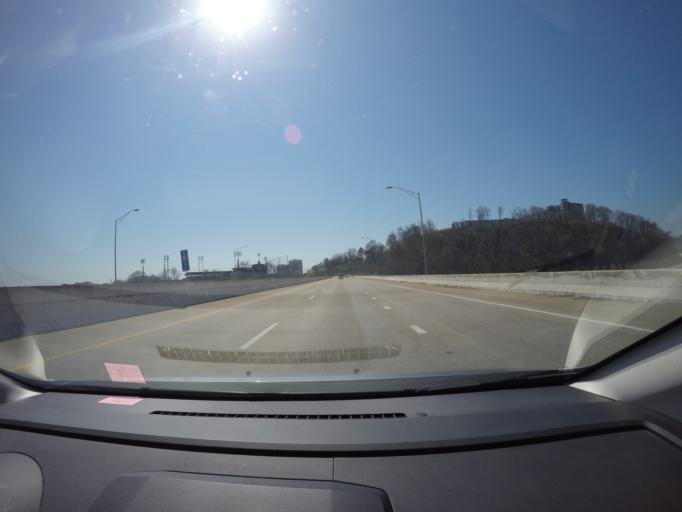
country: US
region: Tennessee
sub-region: Hamilton County
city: Chattanooga
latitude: 35.0566
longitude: -85.3161
